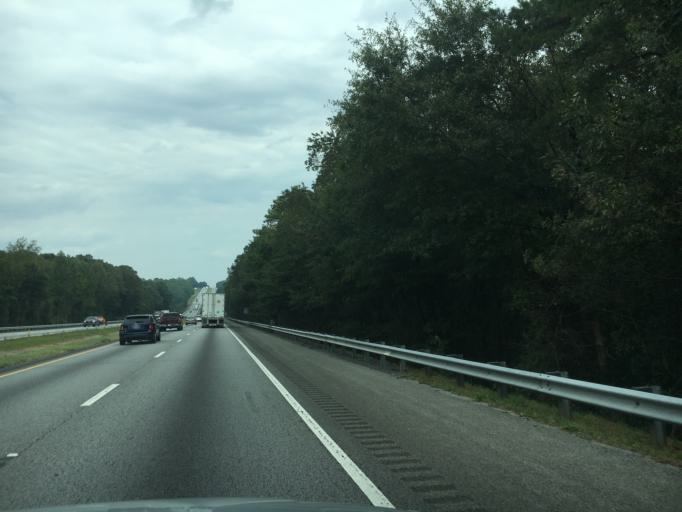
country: US
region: South Carolina
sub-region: Anderson County
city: Centerville
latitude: 34.5499
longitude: -82.7990
